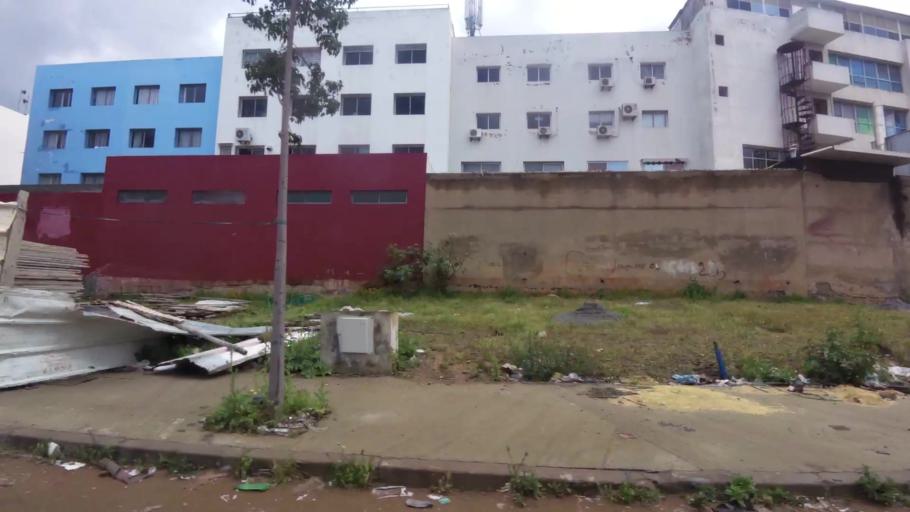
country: MA
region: Grand Casablanca
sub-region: Nouaceur
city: Bouskoura
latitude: 33.5185
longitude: -7.6498
